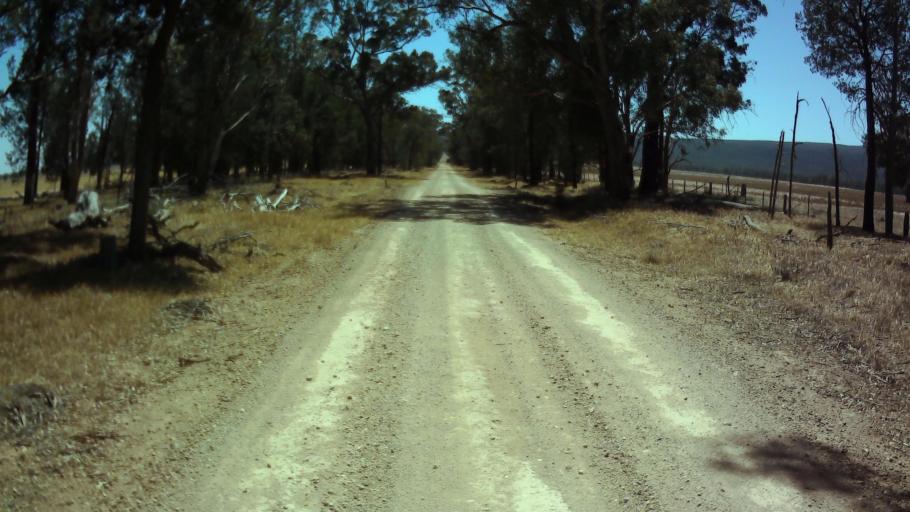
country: AU
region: New South Wales
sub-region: Weddin
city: Grenfell
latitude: -33.9996
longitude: 147.9570
